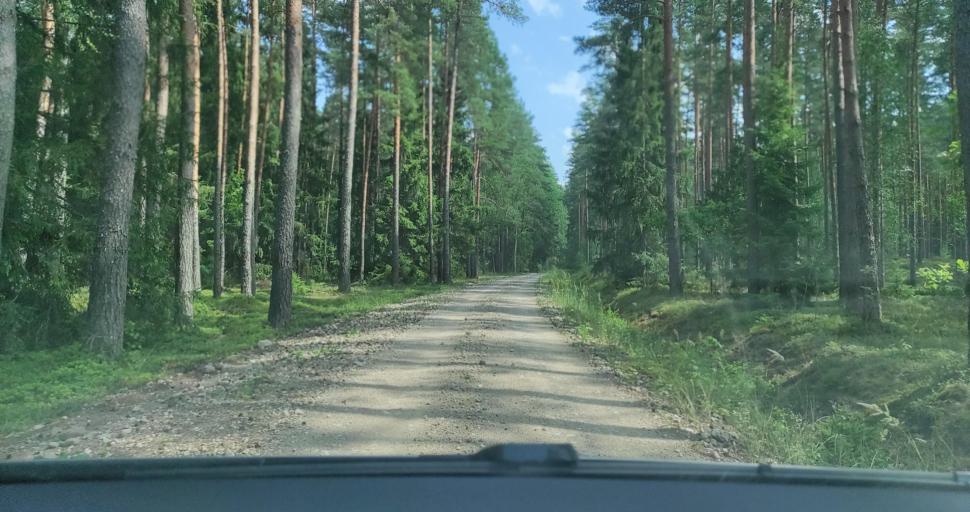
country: LV
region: Kuldigas Rajons
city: Kuldiga
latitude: 57.0676
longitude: 22.2215
